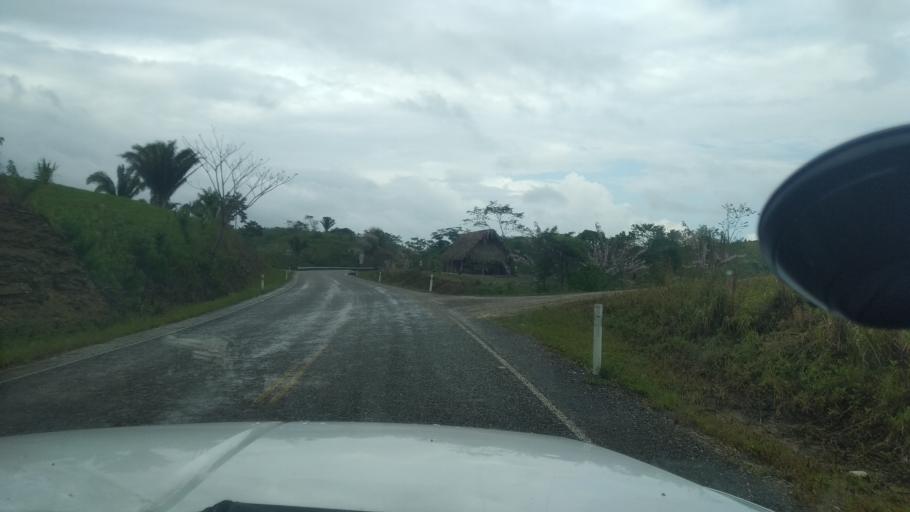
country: GT
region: Peten
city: San Luis
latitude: 16.1844
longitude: -89.1976
